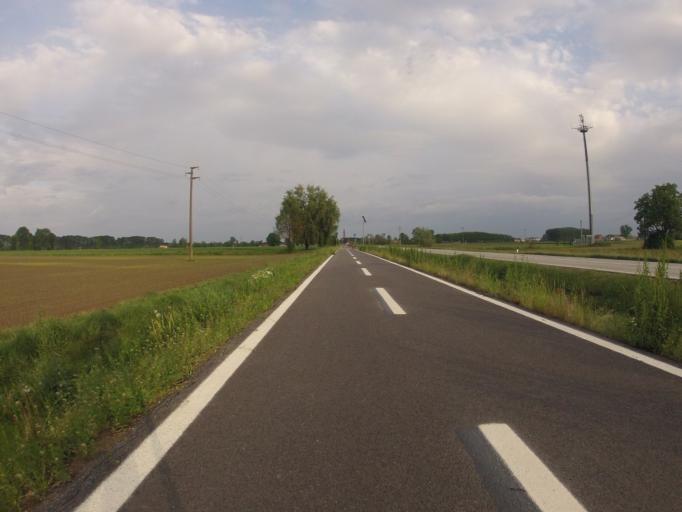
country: IT
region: Piedmont
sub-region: Provincia di Torino
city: Villafranca Piemonte
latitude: 44.7747
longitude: 7.5199
